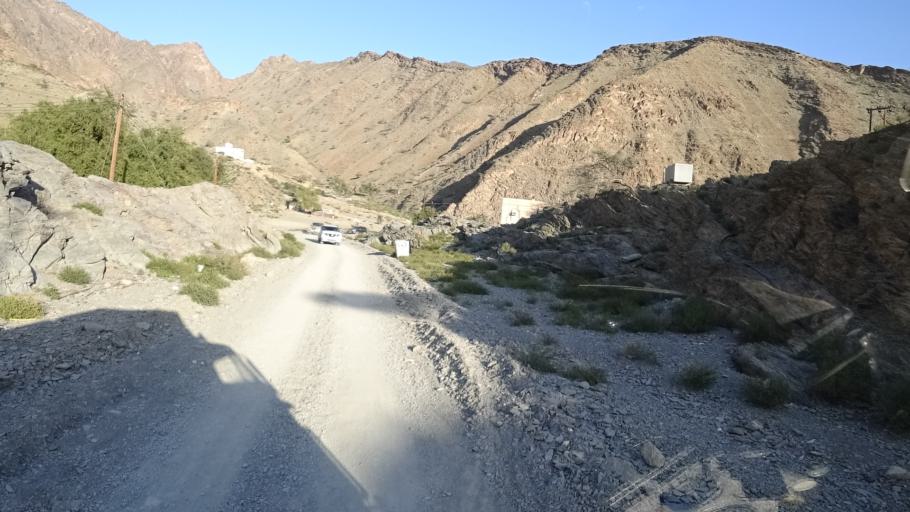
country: OM
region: Al Batinah
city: Rustaq
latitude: 23.2667
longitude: 57.3977
